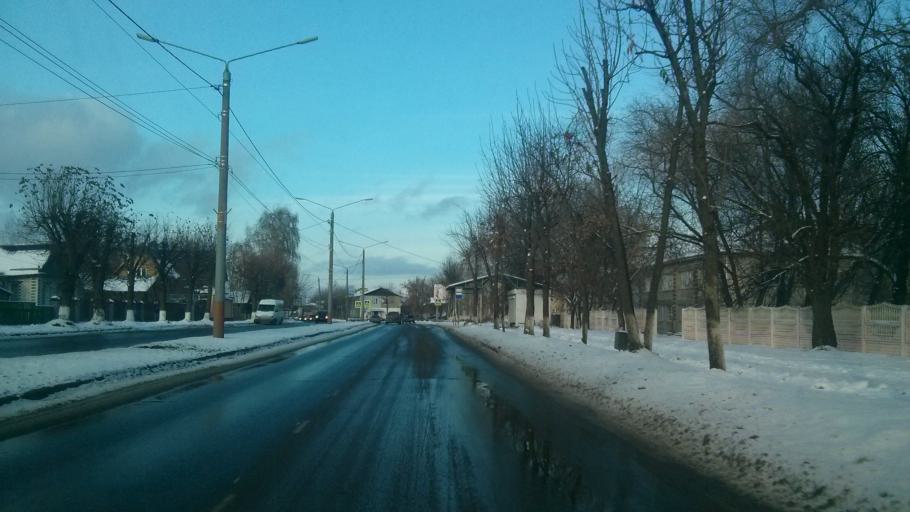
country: RU
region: Vladimir
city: Murom
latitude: 55.5825
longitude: 42.0366
